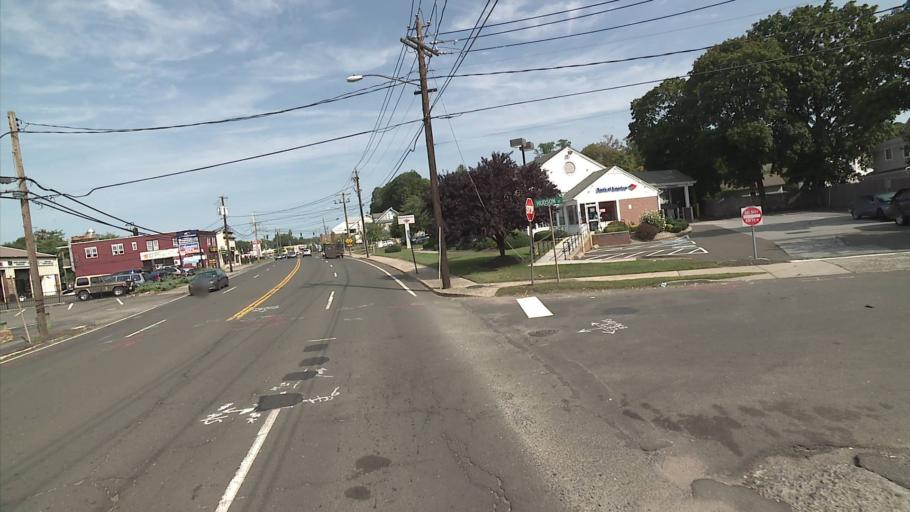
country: US
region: Connecticut
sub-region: Fairfield County
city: Norwalk
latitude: 41.1291
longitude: -73.4225
